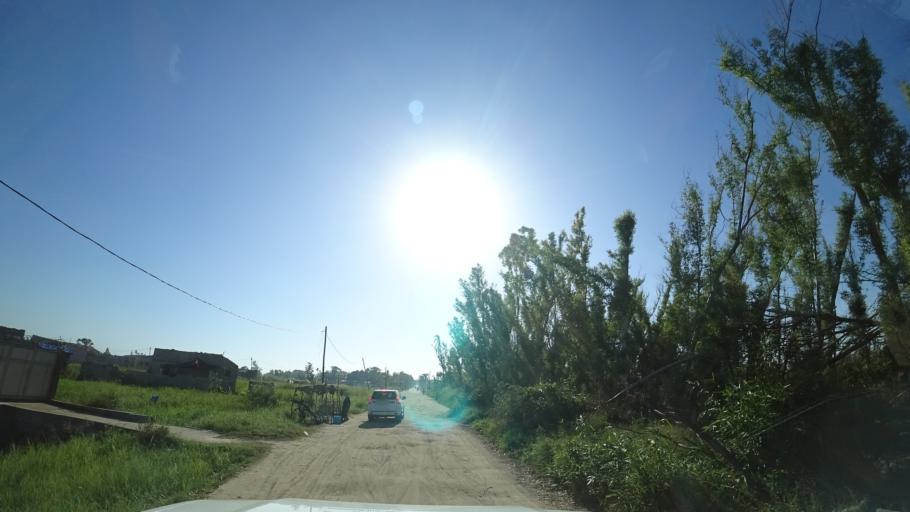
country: MZ
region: Sofala
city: Beira
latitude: -19.7694
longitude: 34.8900
